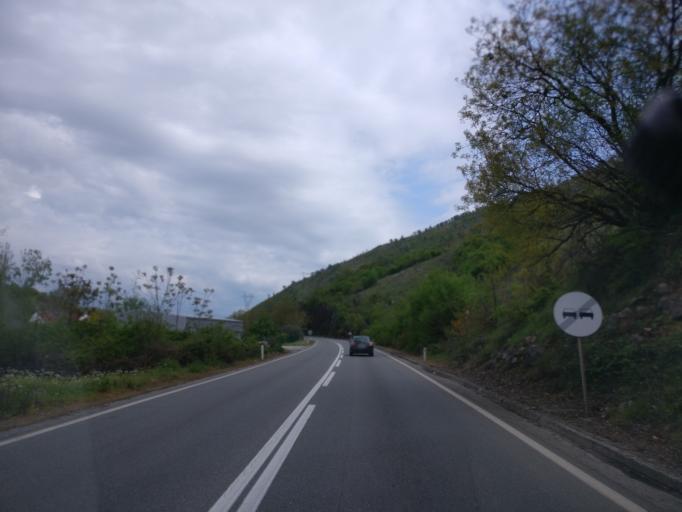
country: ME
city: Spuz
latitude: 42.4581
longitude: 19.1802
